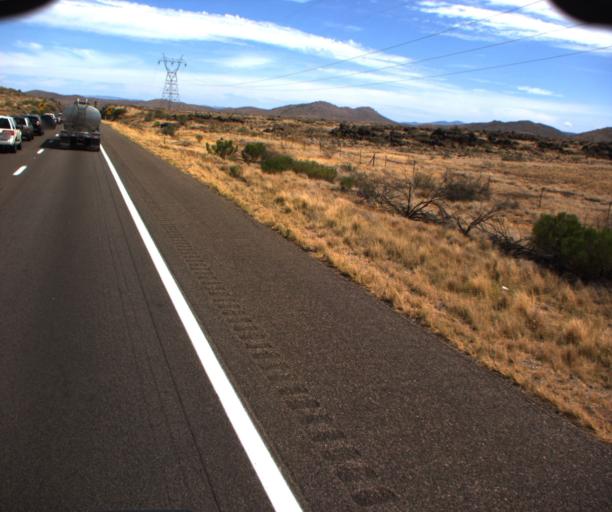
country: US
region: Arizona
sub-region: Yavapai County
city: Cordes Lakes
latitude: 34.2222
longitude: -112.1107
